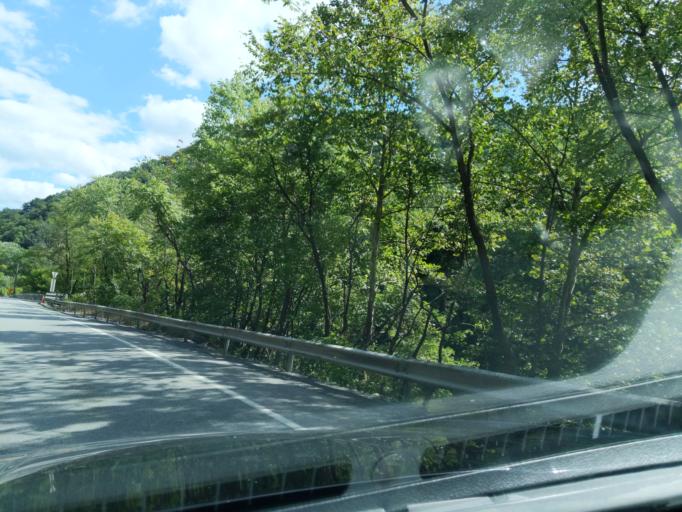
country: US
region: Pennsylvania
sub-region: Blair County
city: Tyrone
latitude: 40.6666
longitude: -78.2292
